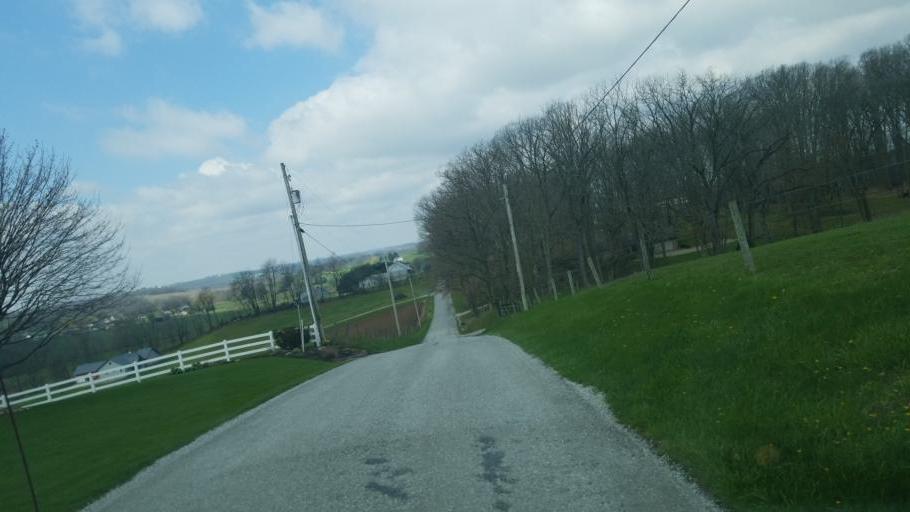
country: US
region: Ohio
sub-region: Holmes County
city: Millersburg
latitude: 40.6129
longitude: -81.8064
